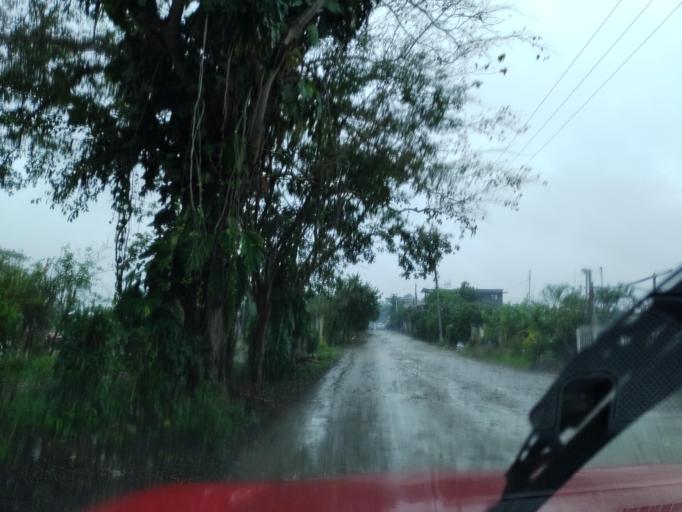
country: MX
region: Veracruz
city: Agua Dulce
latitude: 20.3627
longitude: -97.3293
